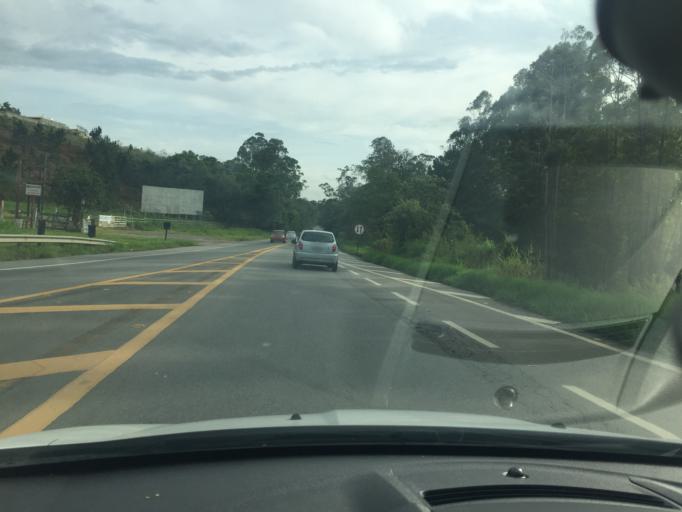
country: BR
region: Sao Paulo
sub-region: Campo Limpo Paulista
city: Campo Limpo Paulista
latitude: -23.1793
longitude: -46.7769
